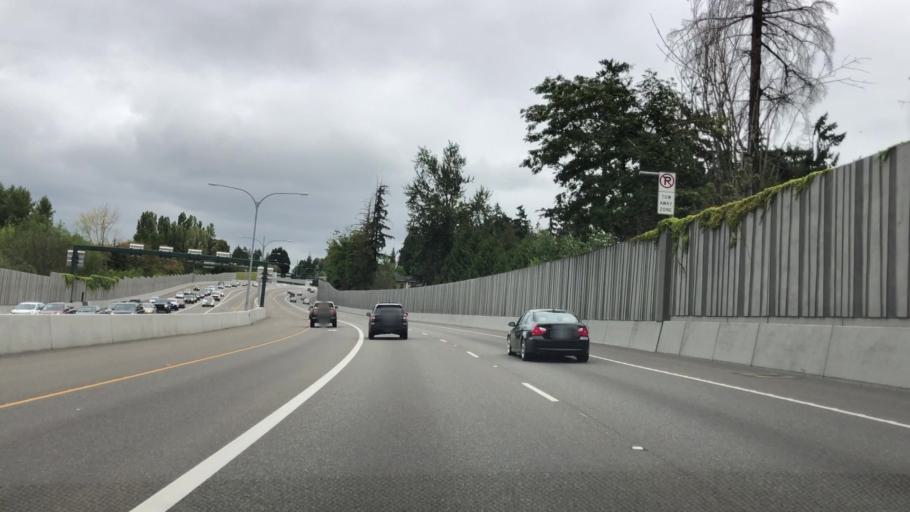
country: US
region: Washington
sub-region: King County
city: Clyde Hill
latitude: 47.6368
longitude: -122.2233
